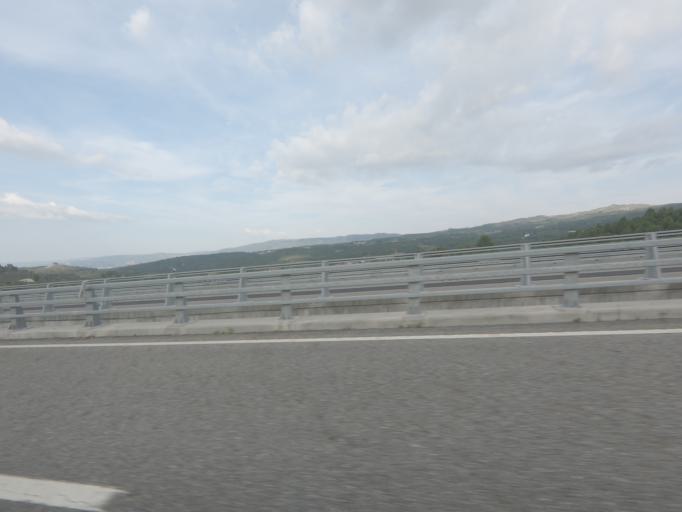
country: PT
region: Vila Real
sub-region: Chaves
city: Chaves
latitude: 41.6999
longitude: -7.5514
